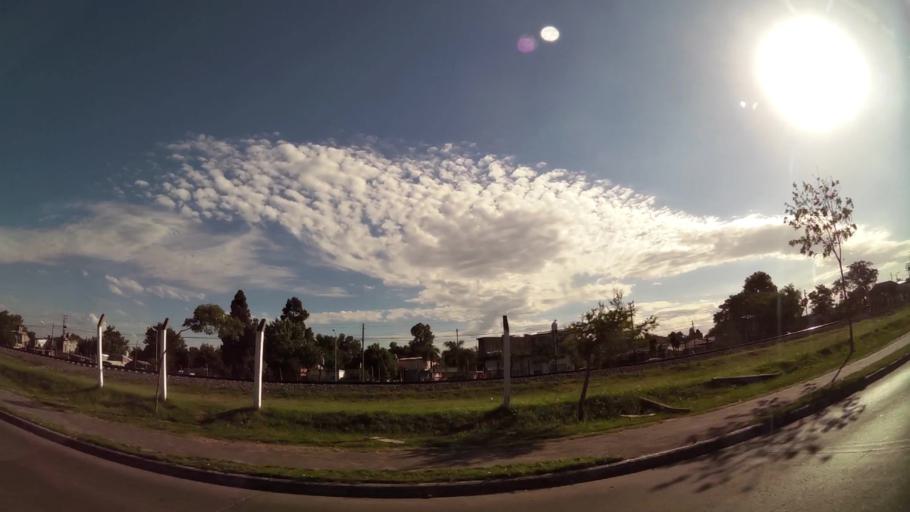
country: AR
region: Buenos Aires
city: Santa Catalina - Dique Lujan
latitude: -34.4885
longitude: -58.7178
